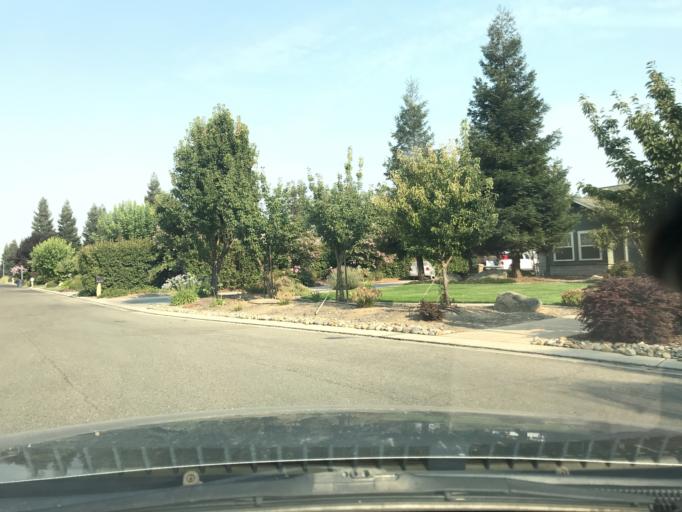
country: US
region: California
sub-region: Merced County
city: Atwater
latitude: 37.3193
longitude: -120.6020
